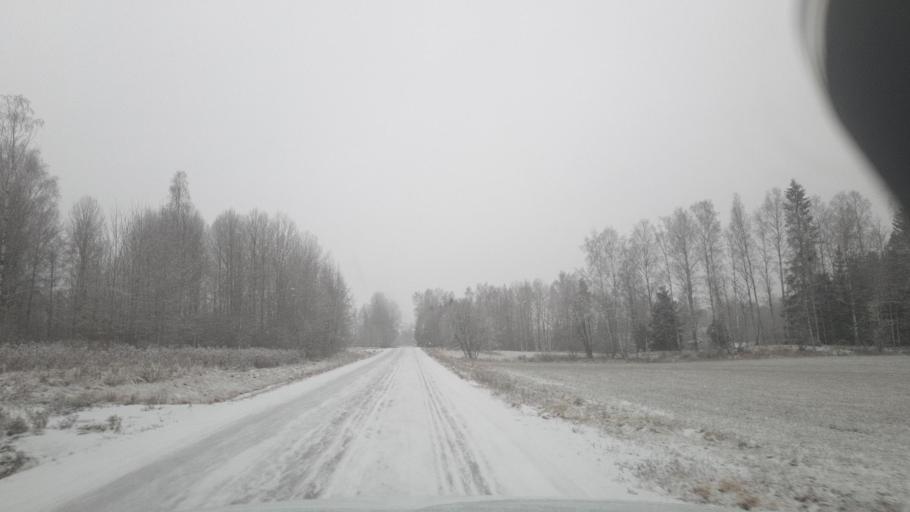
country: SE
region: Vaermland
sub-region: Grums Kommun
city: Slottsbron
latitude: 59.4621
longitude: 12.8766
